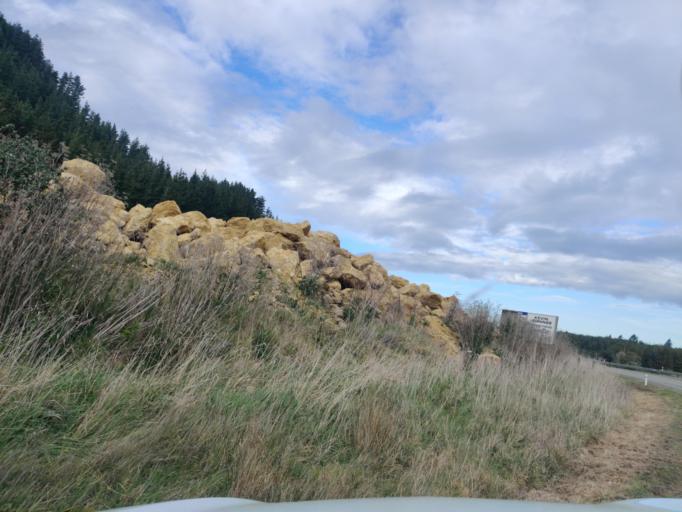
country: NZ
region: Manawatu-Wanganui
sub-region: Palmerston North City
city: Palmerston North
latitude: -40.3346
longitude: 175.8175
